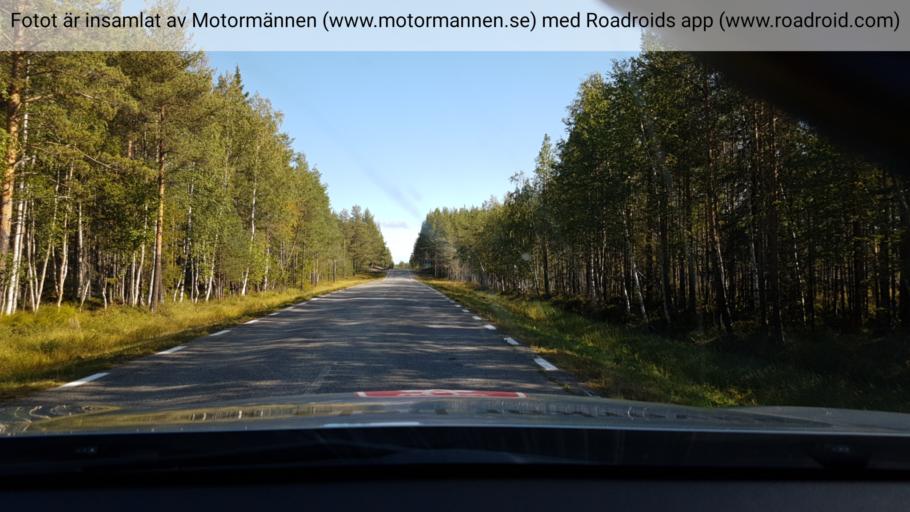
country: SE
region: Vaesterbotten
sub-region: Norsjo Kommun
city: Norsjoe
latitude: 65.1363
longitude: 19.2863
